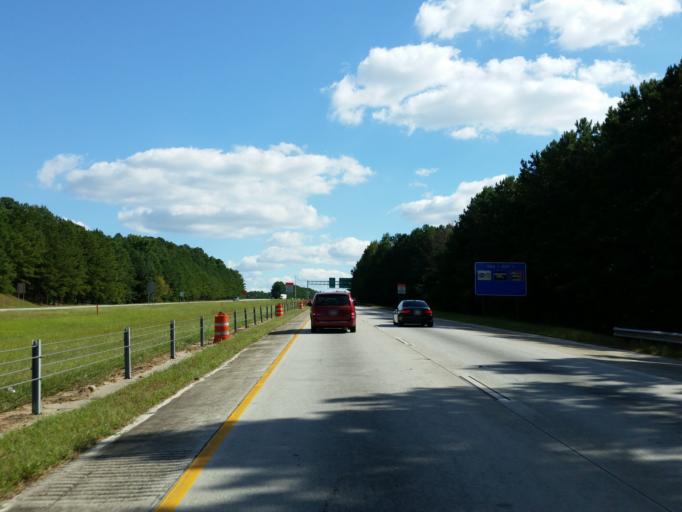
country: US
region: Georgia
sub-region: Henry County
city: Stockbridge
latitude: 33.5609
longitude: -84.2715
